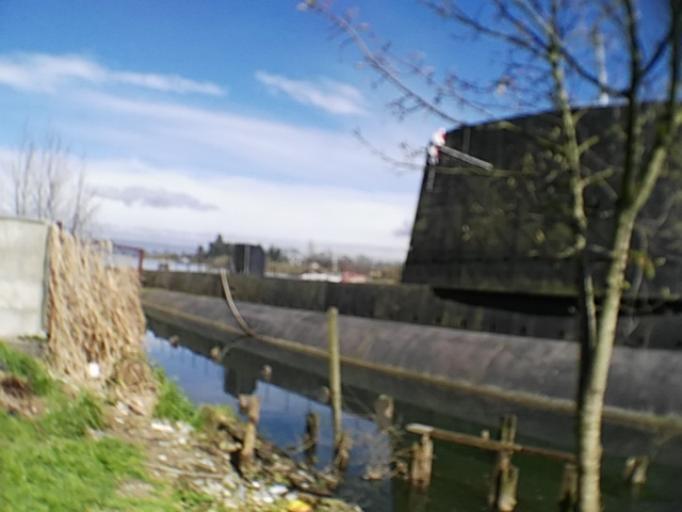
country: CL
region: Los Rios
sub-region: Provincia de Valdivia
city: Valdivia
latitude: -39.8160
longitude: -73.2490
